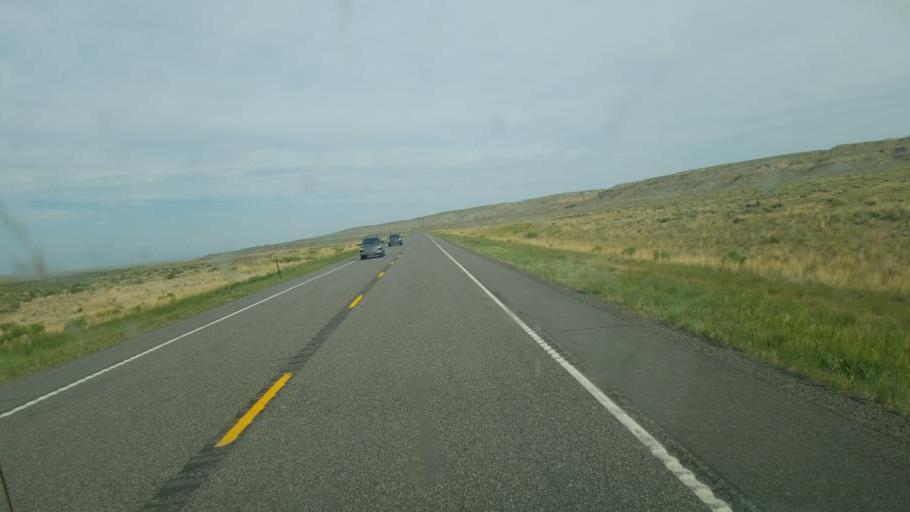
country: US
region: Wyoming
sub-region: Fremont County
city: Riverton
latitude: 43.2181
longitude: -107.9616
